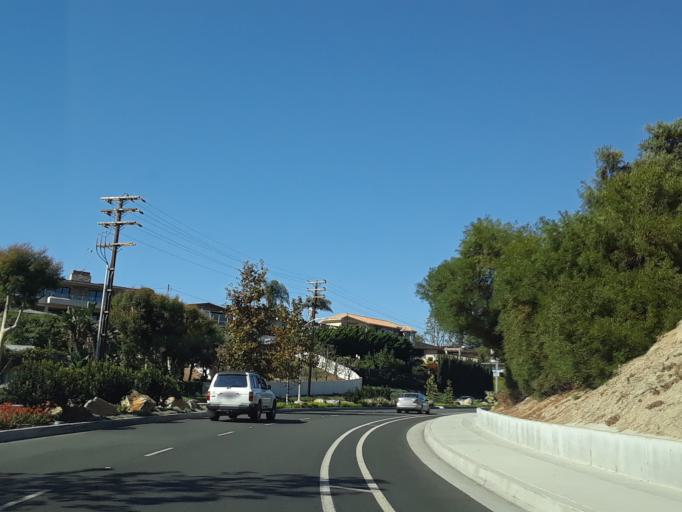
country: US
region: California
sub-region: Orange County
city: Newport Beach
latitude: 33.6195
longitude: -117.9075
